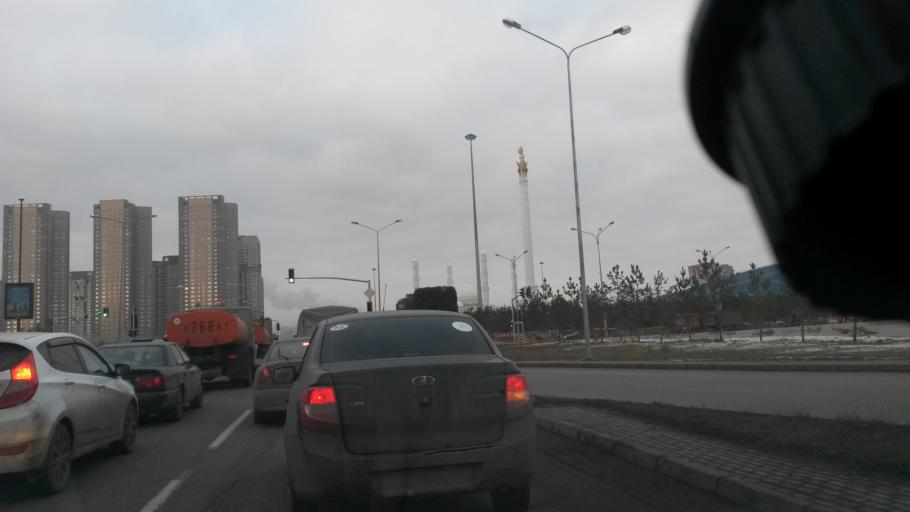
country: KZ
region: Astana Qalasy
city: Astana
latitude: 51.1193
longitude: 71.4672
